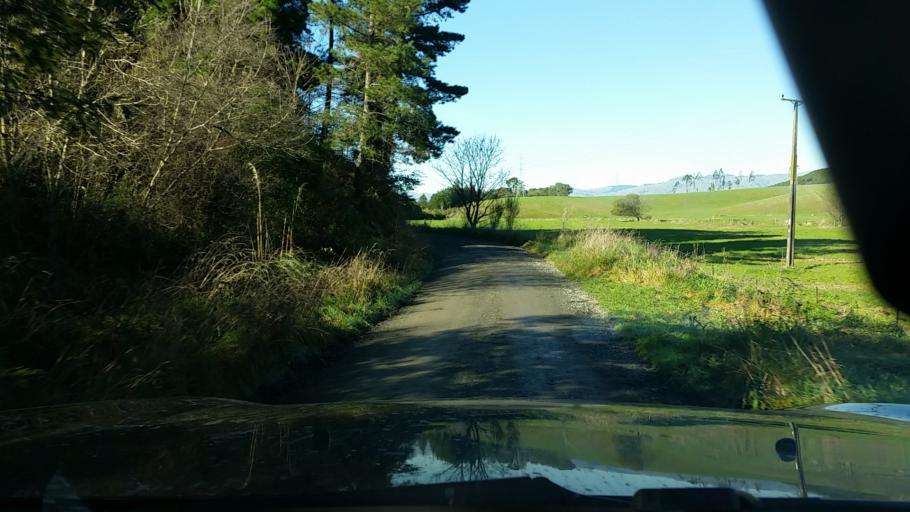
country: NZ
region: Marlborough
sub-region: Marlborough District
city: Blenheim
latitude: -41.4627
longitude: 173.7913
